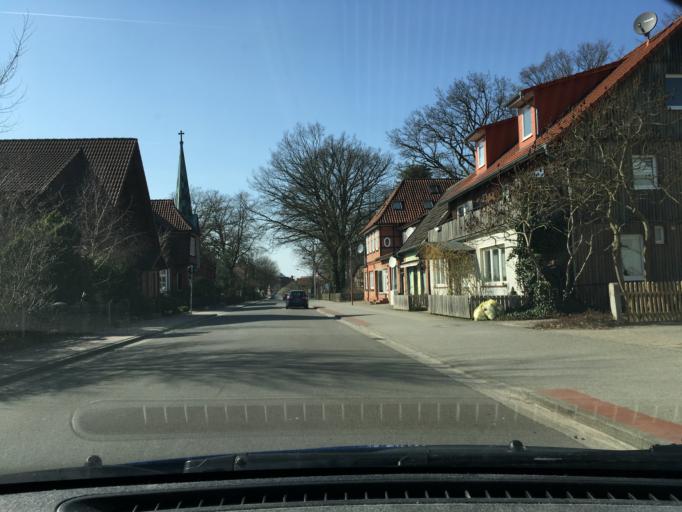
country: DE
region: Lower Saxony
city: Hermannsburg
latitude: 52.8302
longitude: 10.0971
